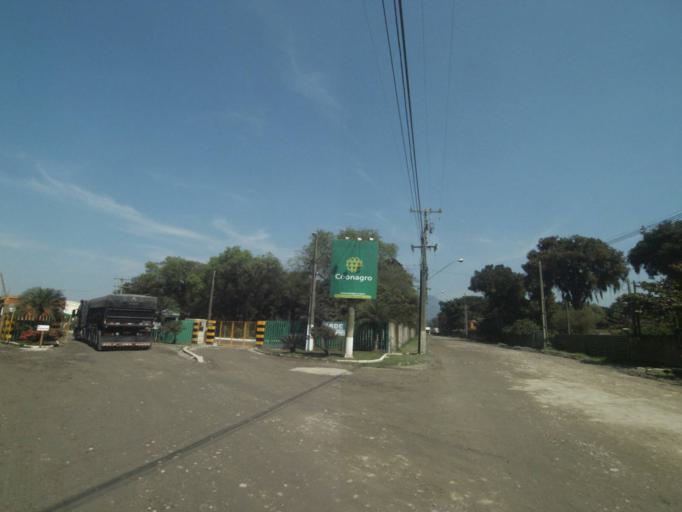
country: BR
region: Parana
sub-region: Paranagua
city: Paranagua
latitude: -25.5477
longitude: -48.5755
